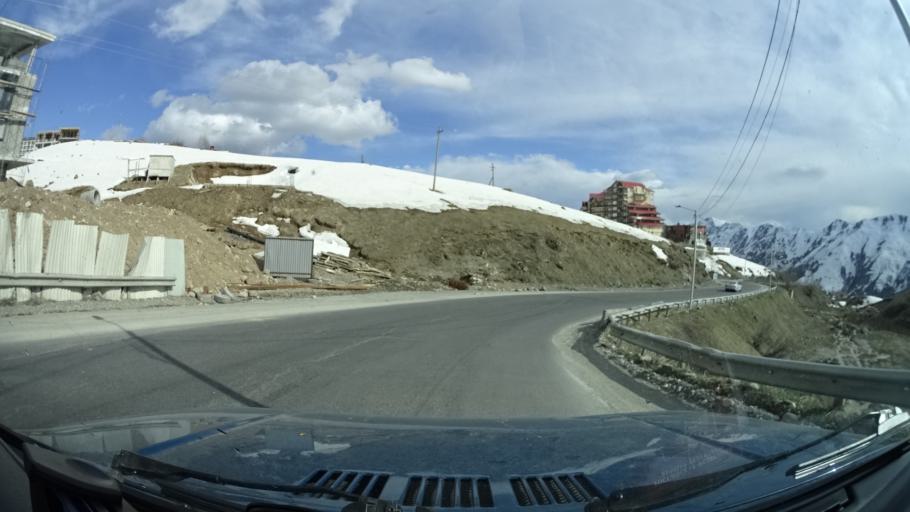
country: GE
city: Gudauri
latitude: 42.4701
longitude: 44.4805
